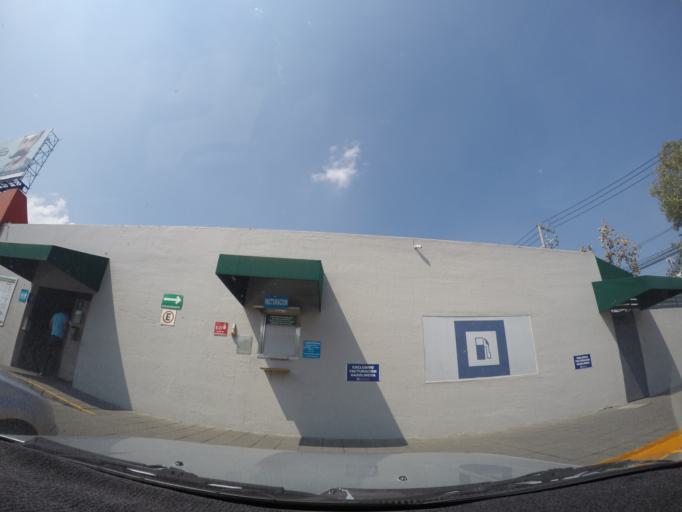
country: MX
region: Jalisco
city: Las Pintas de Arriba
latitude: 20.5855
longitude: -103.3303
